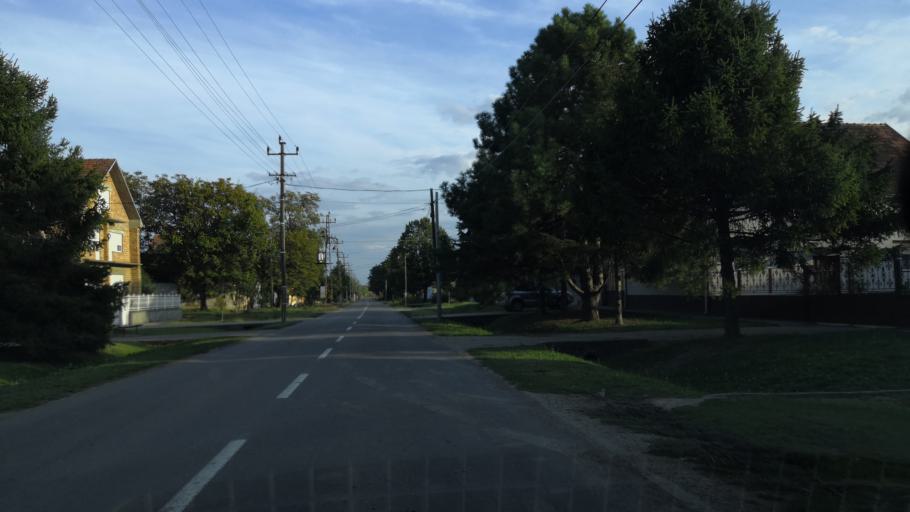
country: RS
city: Novi Karlovci
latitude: 45.0730
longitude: 20.1833
